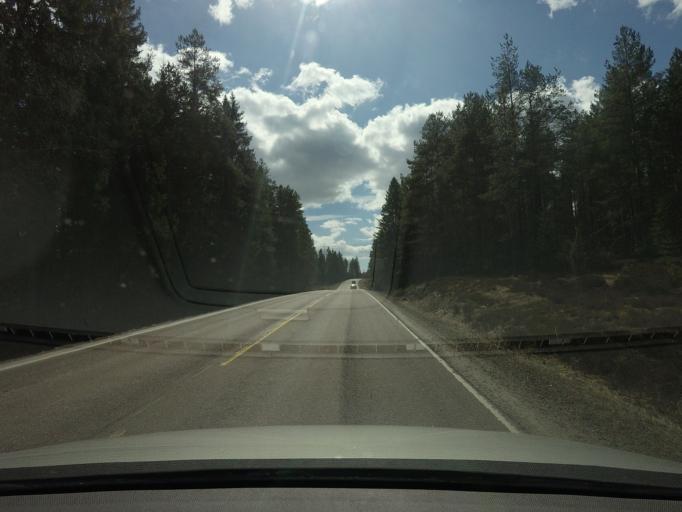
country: FI
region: Kymenlaakso
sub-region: Kotka-Hamina
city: Hamina
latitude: 60.6666
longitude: 27.2683
